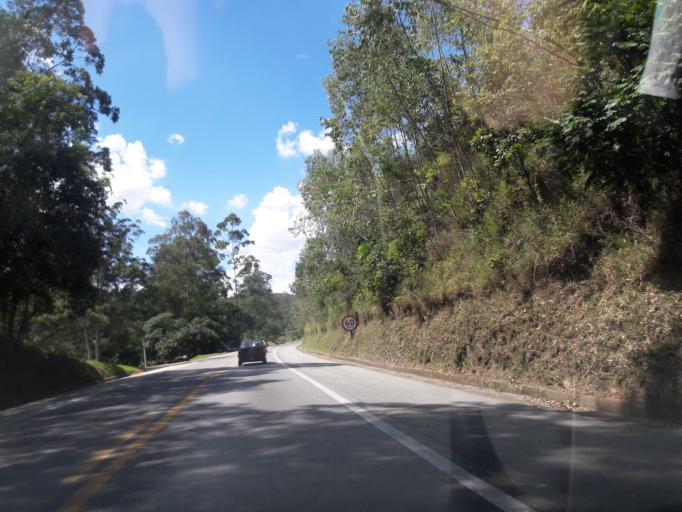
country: BR
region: Sao Paulo
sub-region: Francisco Morato
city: Francisco Morato
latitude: -23.2794
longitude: -46.7951
